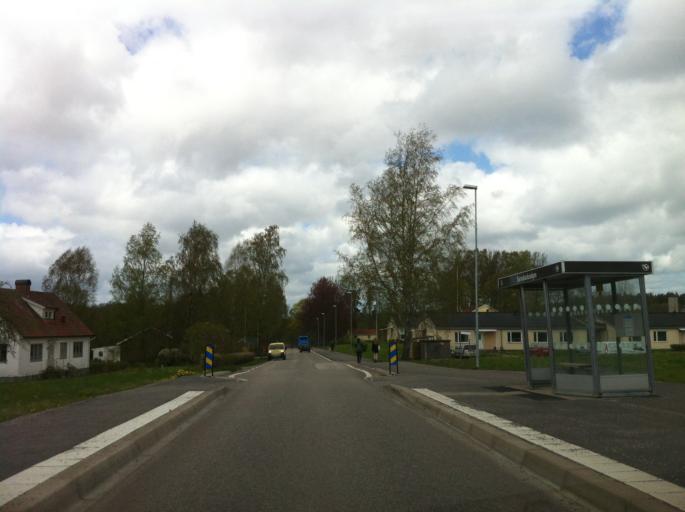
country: SE
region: Vaestra Goetaland
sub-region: Alingsas Kommun
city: Ingared
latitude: 57.8454
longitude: 12.4854
